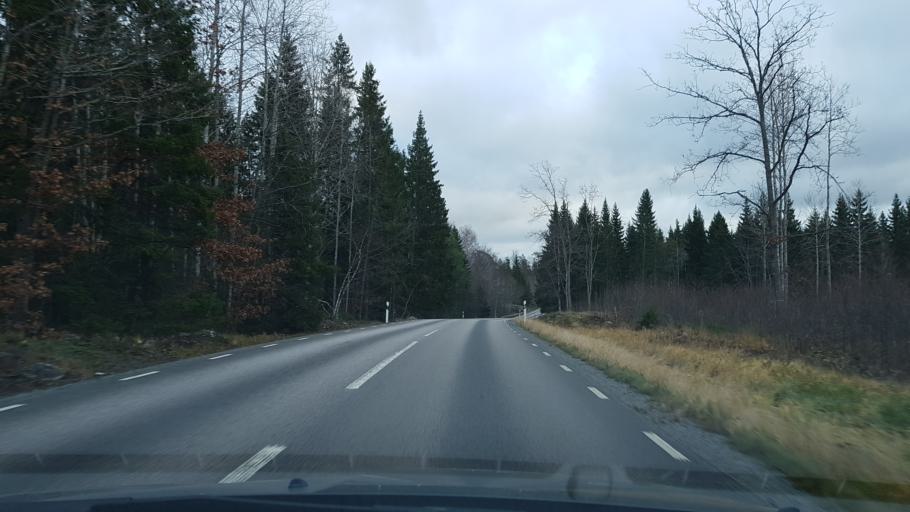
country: SE
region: Stockholm
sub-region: Norrtalje Kommun
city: Skanninge
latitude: 60.0342
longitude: 18.4518
